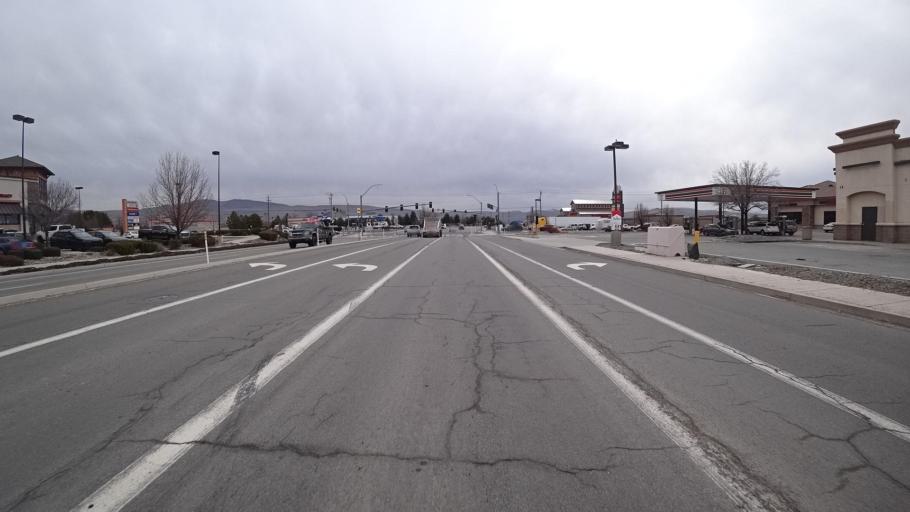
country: US
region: Nevada
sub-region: Washoe County
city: Spanish Springs
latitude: 39.6390
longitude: -119.7129
